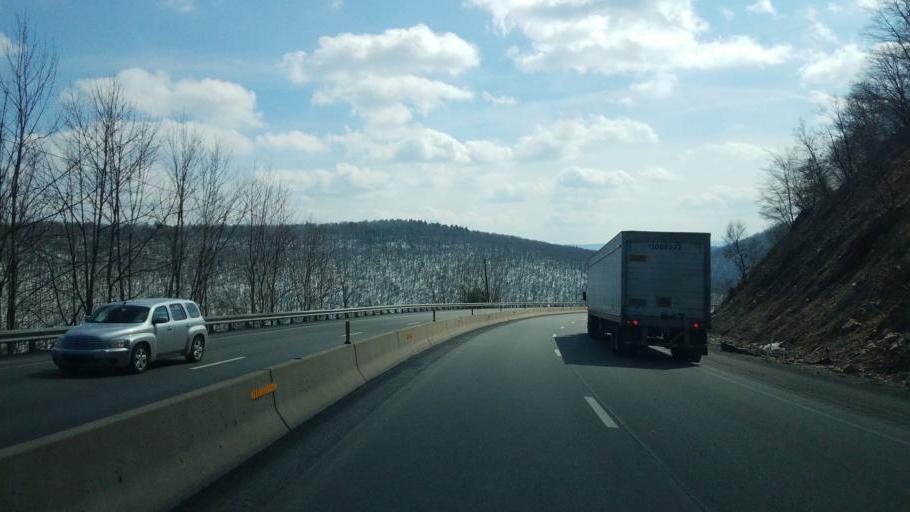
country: US
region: Pennsylvania
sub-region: Mifflin County
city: Milroy
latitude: 40.7438
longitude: -77.6253
